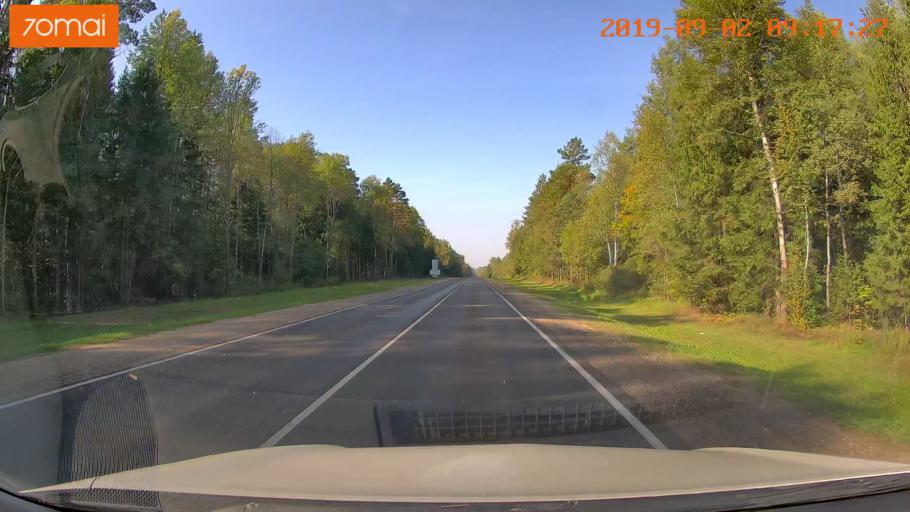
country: RU
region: Kaluga
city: Nikola-Lenivets
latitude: 54.8243
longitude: 35.4516
